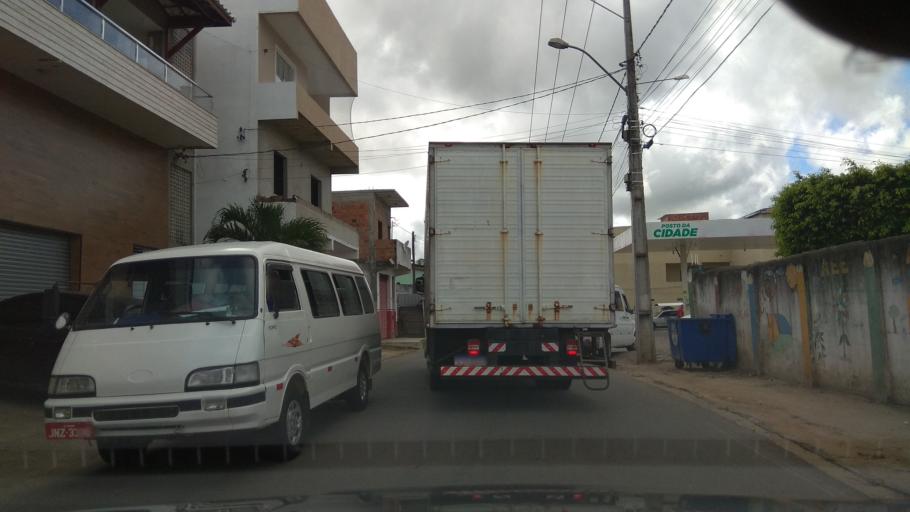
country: BR
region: Bahia
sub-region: Mutuipe
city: Mutuipe
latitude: -13.1772
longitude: -39.4116
